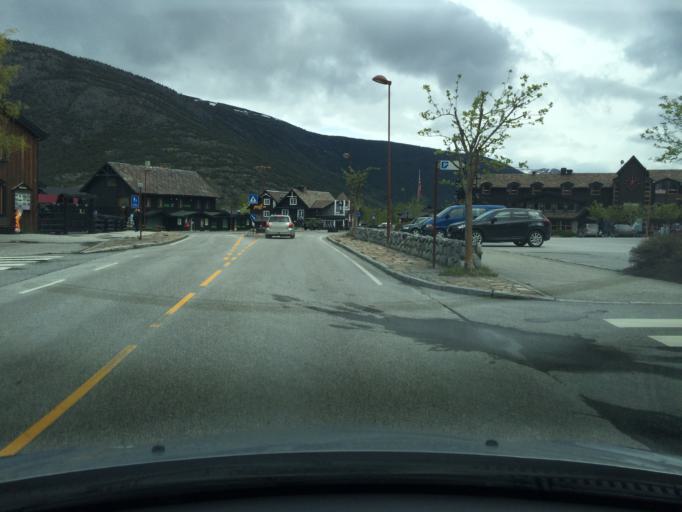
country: NO
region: Oppland
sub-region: Lom
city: Fossbergom
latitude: 61.8371
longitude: 8.5677
